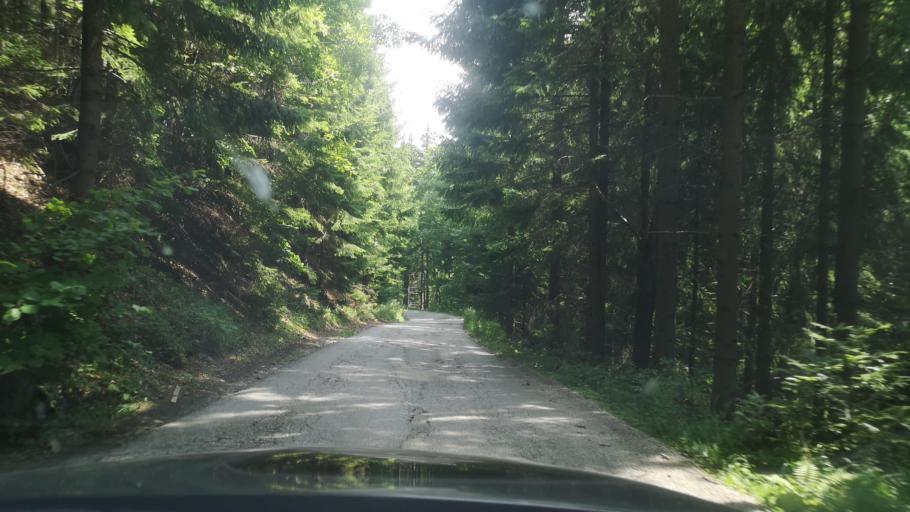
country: SK
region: Zilinsky
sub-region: Okres Zilina
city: Vrutky
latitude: 49.1045
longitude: 18.8597
